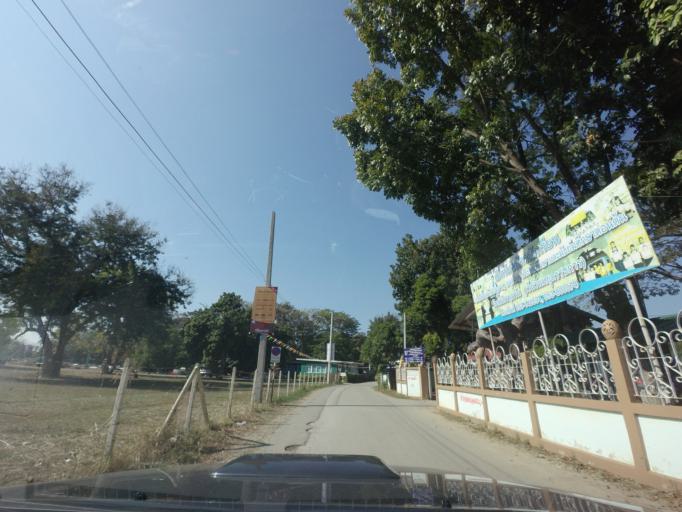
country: TH
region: Chiang Mai
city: Chiang Mai
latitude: 18.7676
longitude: 99.0044
